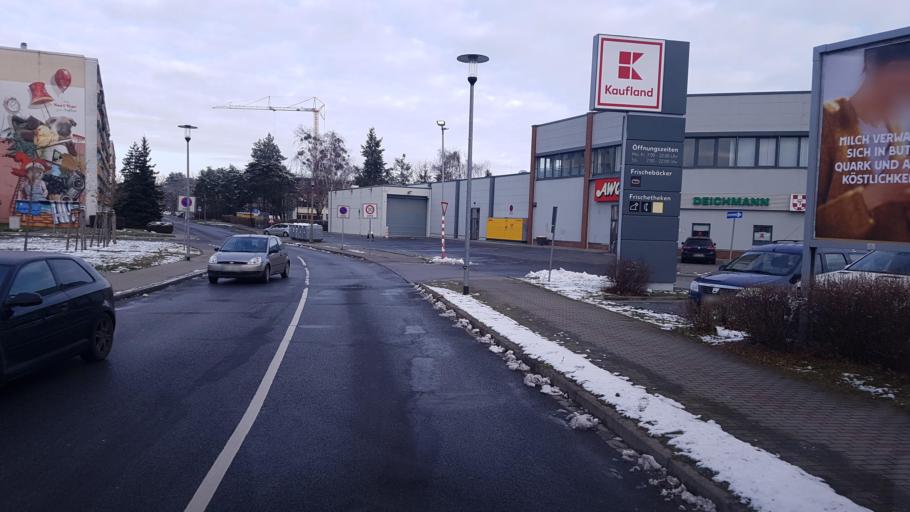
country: DE
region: Brandenburg
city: Strausberg
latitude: 52.5735
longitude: 13.8962
